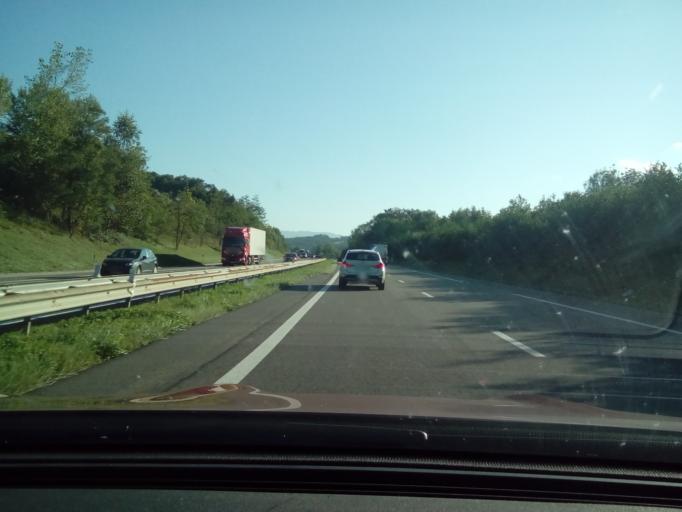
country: FR
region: Rhone-Alpes
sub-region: Departement de la Haute-Savoie
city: Alby-sur-Cheran
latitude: 45.8285
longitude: 6.0389
